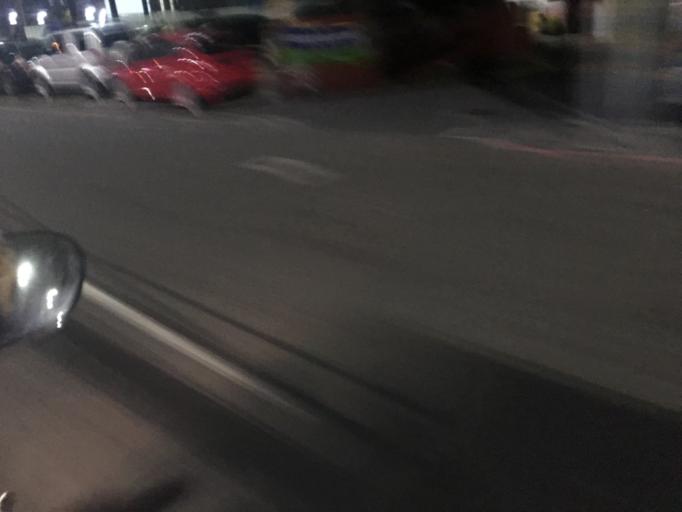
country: TW
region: Taiwan
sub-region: Hsinchu
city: Hsinchu
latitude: 24.8140
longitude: 120.9683
